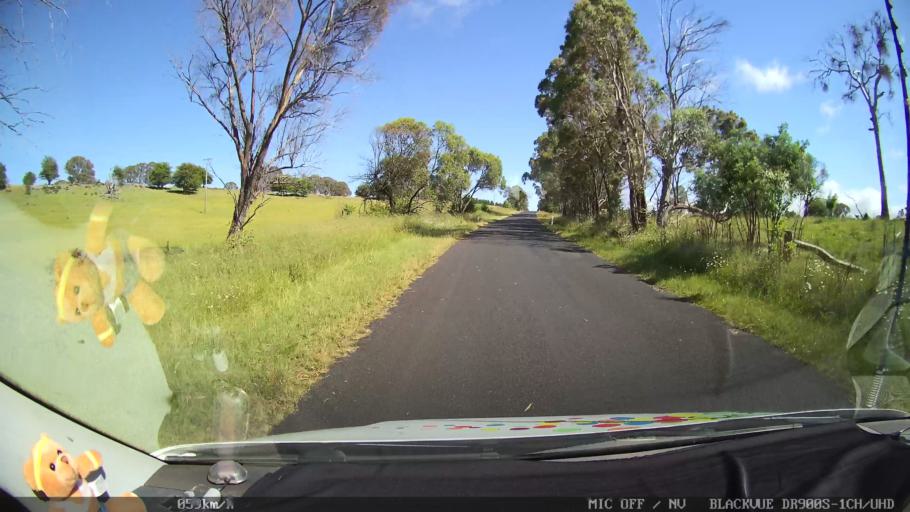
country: AU
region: New South Wales
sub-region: Guyra
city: Guyra
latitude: -30.1070
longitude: 151.6796
